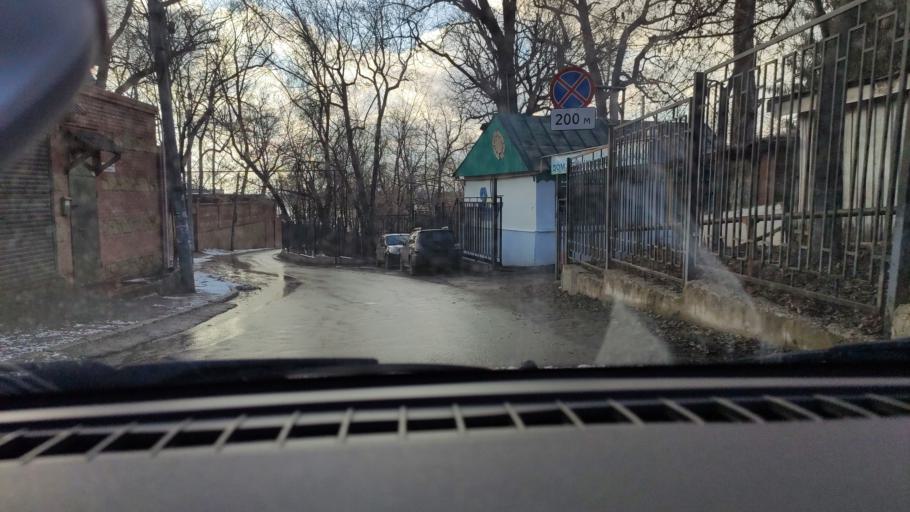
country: RU
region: Samara
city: Samara
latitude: 53.2631
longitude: 50.1853
